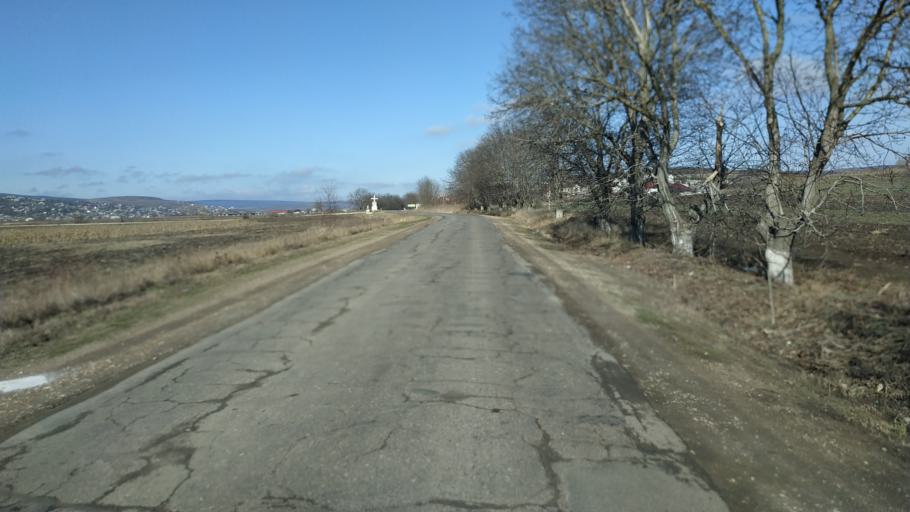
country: MD
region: Laloveni
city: Ialoveni
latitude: 46.9271
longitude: 28.6765
